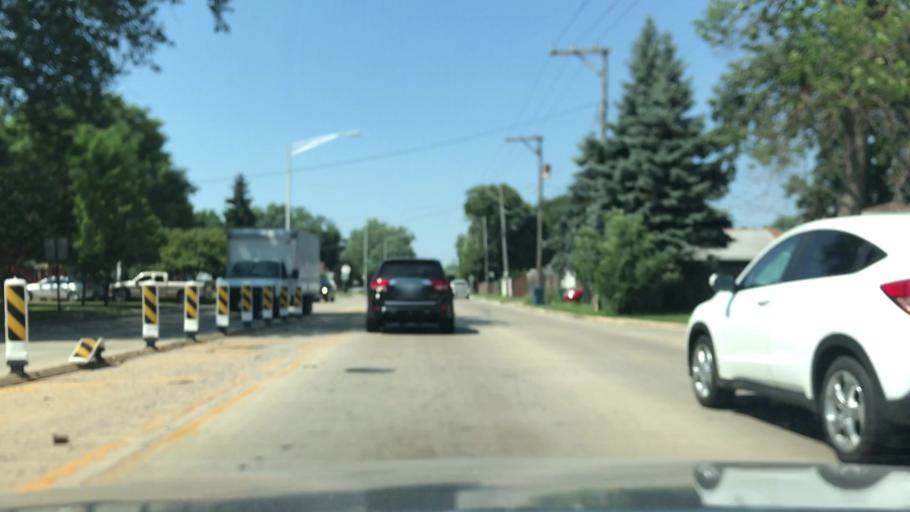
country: US
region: Illinois
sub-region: Cook County
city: Oak Lawn
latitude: 41.7151
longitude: -87.7601
